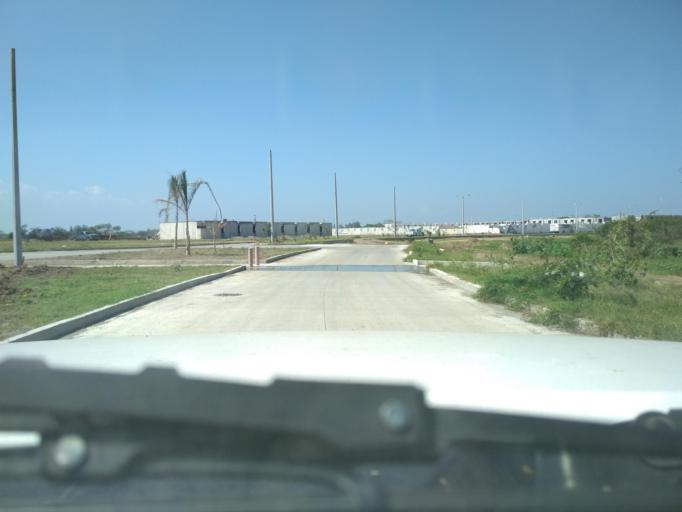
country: MX
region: Veracruz
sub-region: Medellin
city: Fraccionamiento Arboledas San Ramon
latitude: 19.1006
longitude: -96.1666
